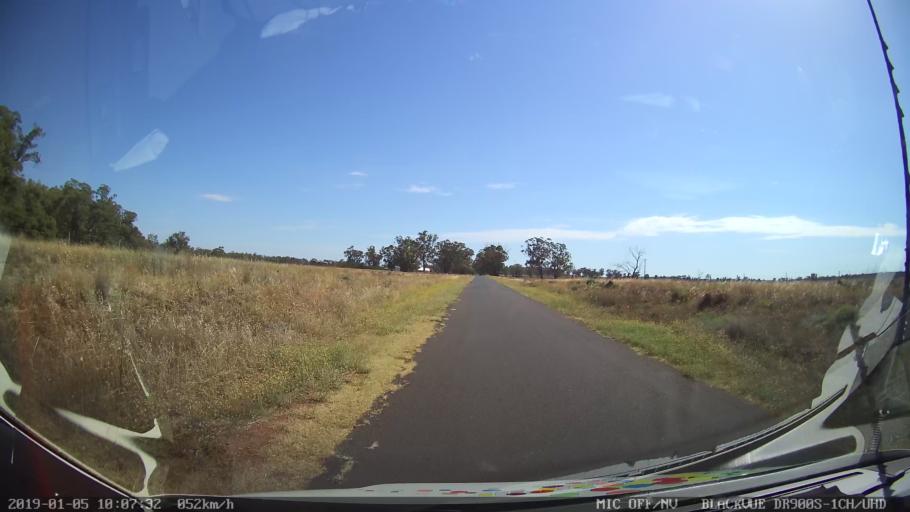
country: AU
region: New South Wales
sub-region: Gilgandra
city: Gilgandra
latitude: -31.6491
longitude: 148.8750
